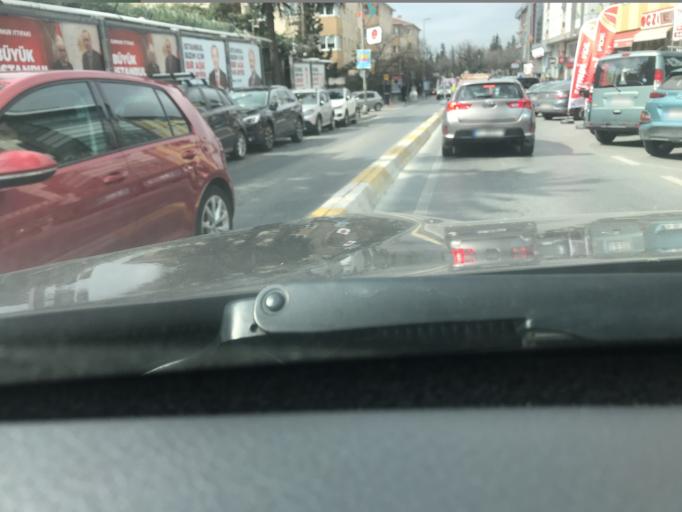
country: TR
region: Istanbul
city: Umraniye
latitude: 41.0327
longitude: 29.1757
